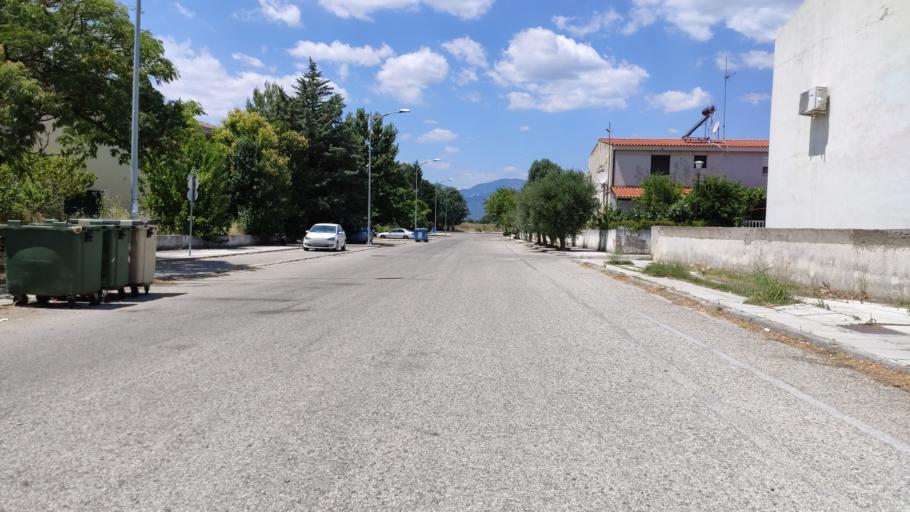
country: GR
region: East Macedonia and Thrace
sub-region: Nomos Rodopis
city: Komotini
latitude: 41.1265
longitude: 25.3961
